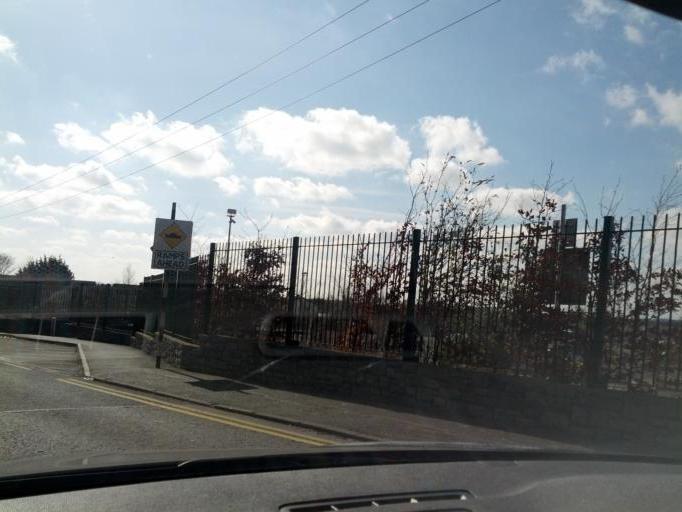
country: IE
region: Leinster
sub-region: Kildare
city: Leixlip
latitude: 53.3695
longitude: -6.5069
